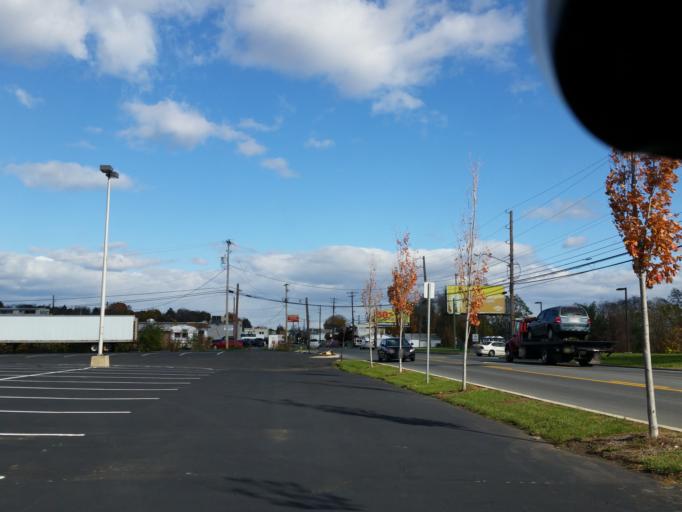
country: US
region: Pennsylvania
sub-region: Cumberland County
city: Lemoyne
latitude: 40.2402
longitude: -76.9046
